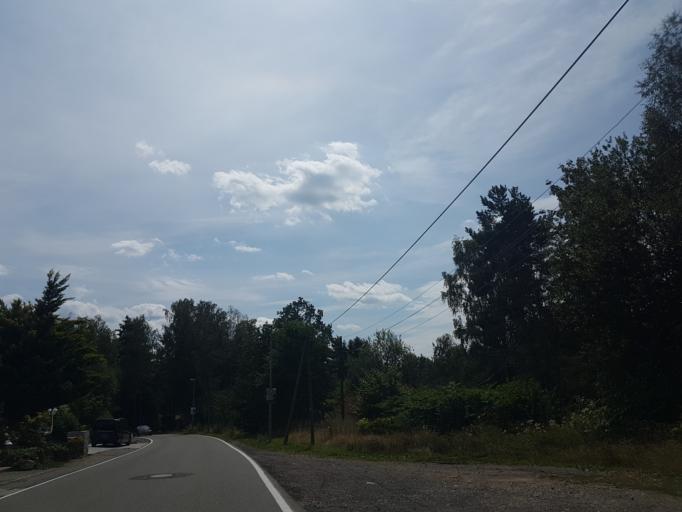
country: DE
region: Saxony
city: Freiberg
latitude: 50.8840
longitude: 13.3554
